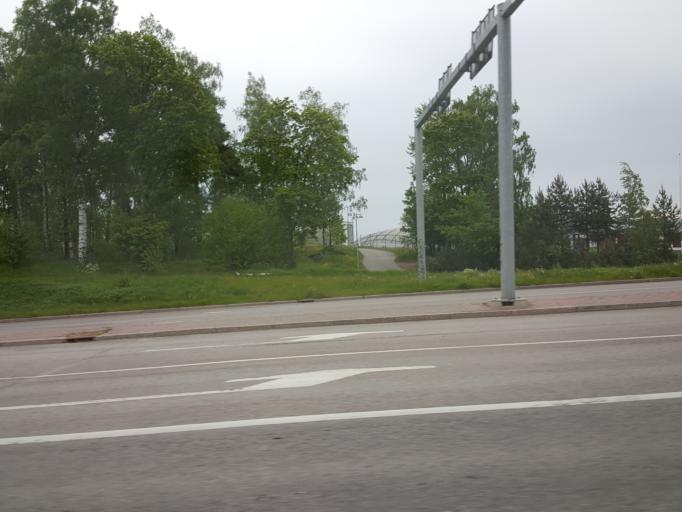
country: FI
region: Uusimaa
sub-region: Helsinki
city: Helsinki
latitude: 60.2047
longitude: 24.9327
